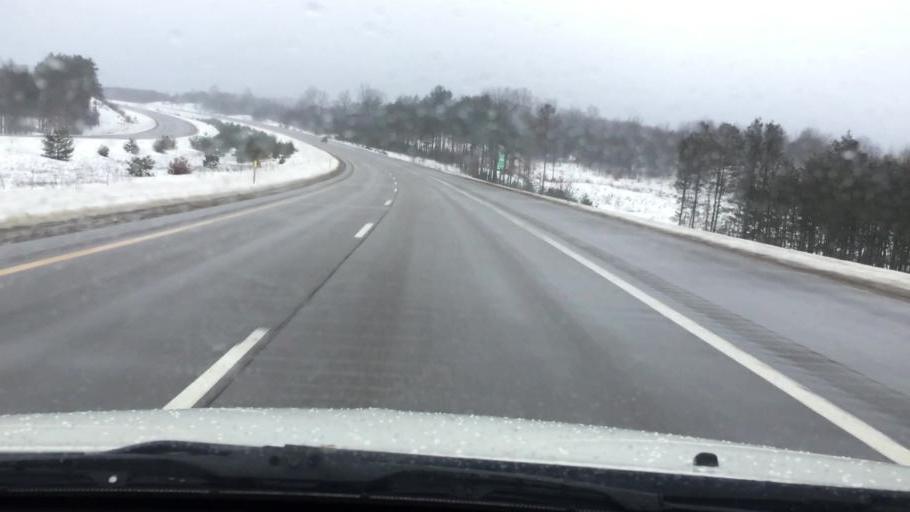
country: US
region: Michigan
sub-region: Wexford County
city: Manton
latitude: 44.3712
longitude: -85.3999
